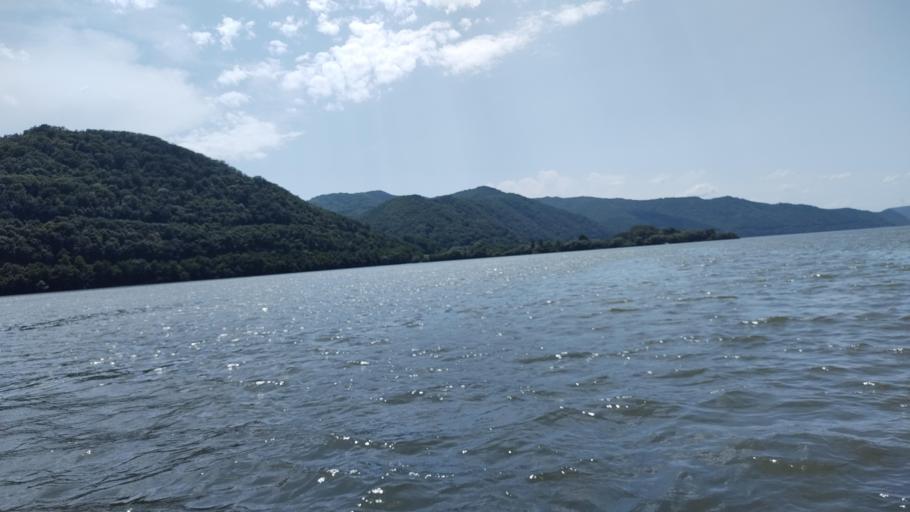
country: RO
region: Caras-Severin
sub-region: Comuna Berzasca
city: Liubcova
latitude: 44.6521
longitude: 21.8561
